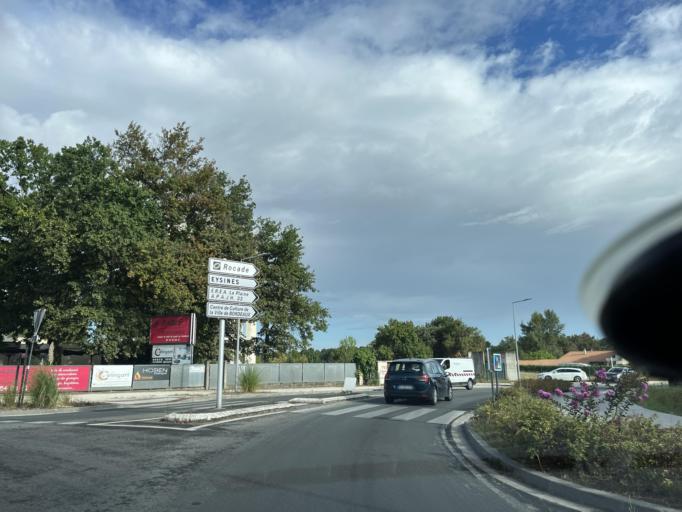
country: FR
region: Aquitaine
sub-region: Departement de la Gironde
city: Le Haillan
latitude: 44.8682
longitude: -0.6631
